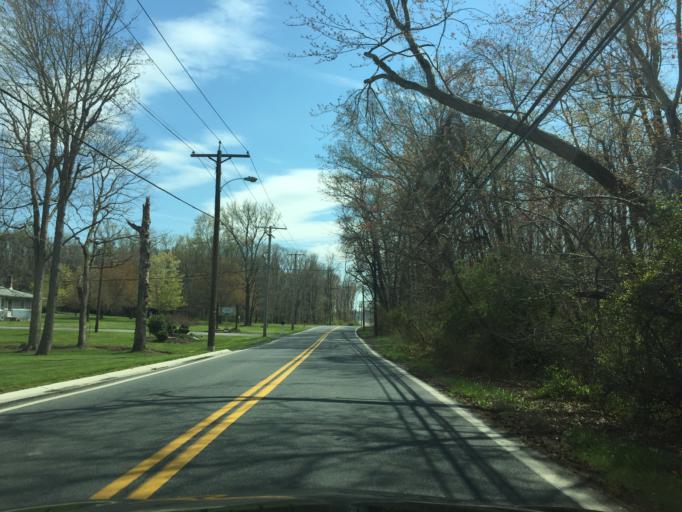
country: US
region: Maryland
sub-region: Baltimore County
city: Edgemere
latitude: 39.2853
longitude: -76.4270
